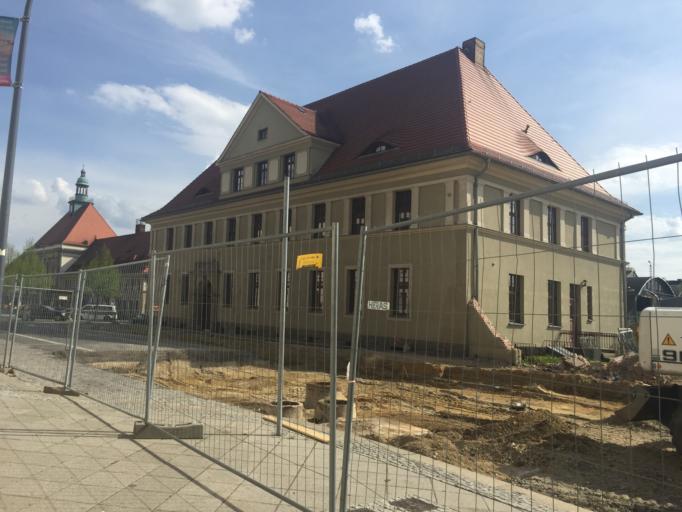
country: DE
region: Saxony
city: Goerlitz
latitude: 51.1484
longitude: 14.9779
